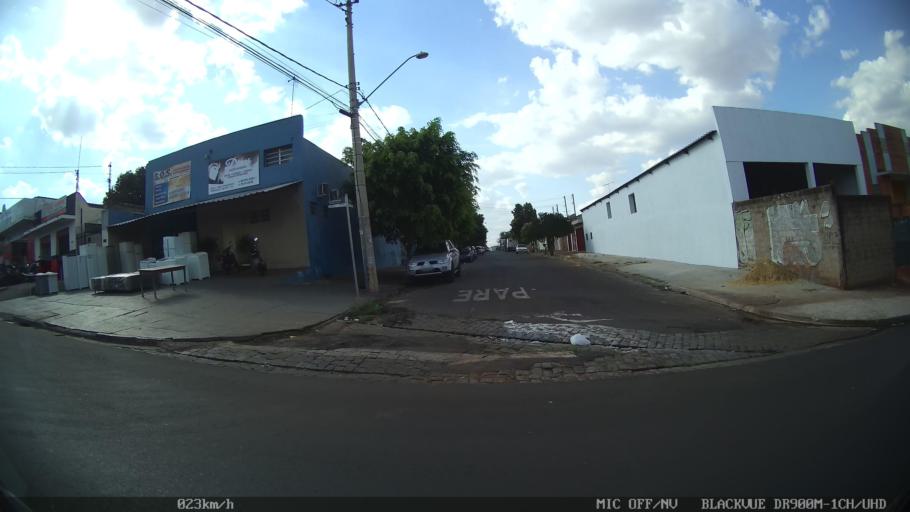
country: BR
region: Sao Paulo
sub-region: Ribeirao Preto
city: Ribeirao Preto
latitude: -21.2021
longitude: -47.8306
